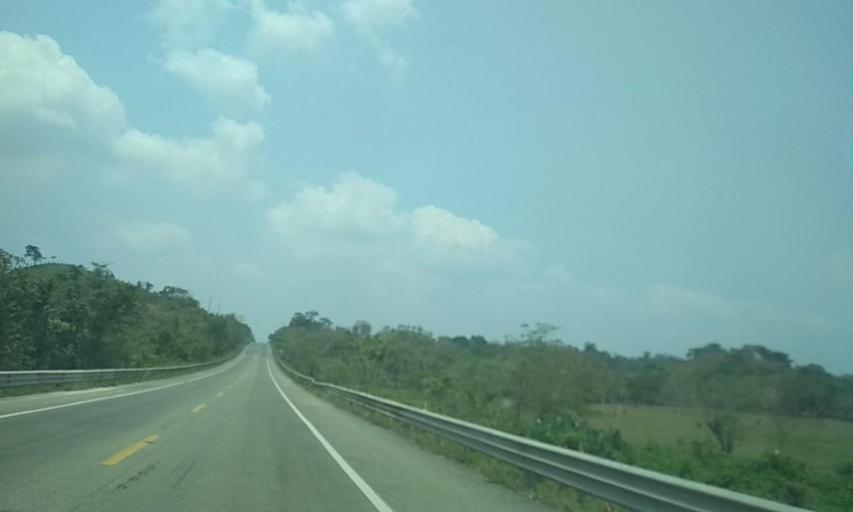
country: MX
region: Tabasco
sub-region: Huimanguillo
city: Francisco Rueda
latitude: 17.6745
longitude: -93.8763
